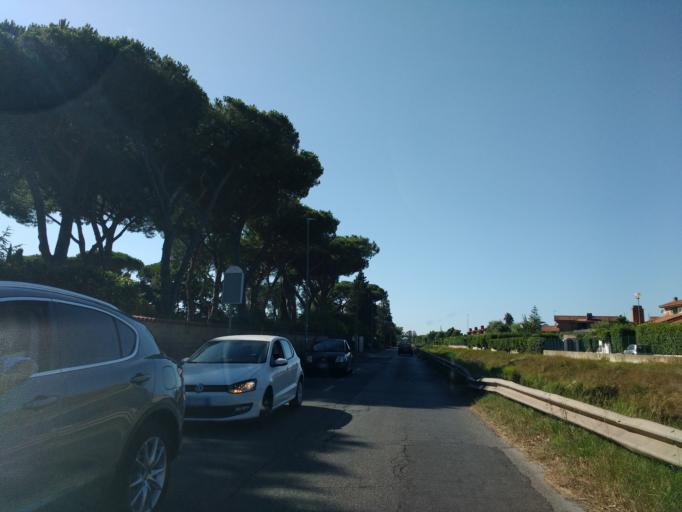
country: IT
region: Latium
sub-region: Citta metropolitana di Roma Capitale
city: Acilia-Castel Fusano-Ostia Antica
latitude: 41.7448
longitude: 12.3363
